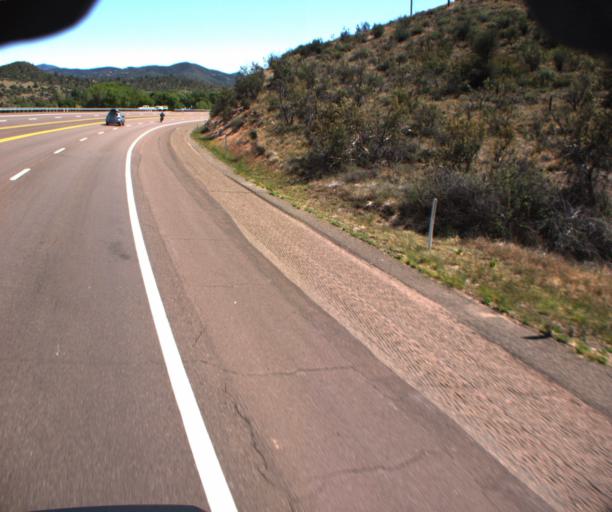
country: US
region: Arizona
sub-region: Yavapai County
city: Prescott
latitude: 34.5870
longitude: -112.4242
